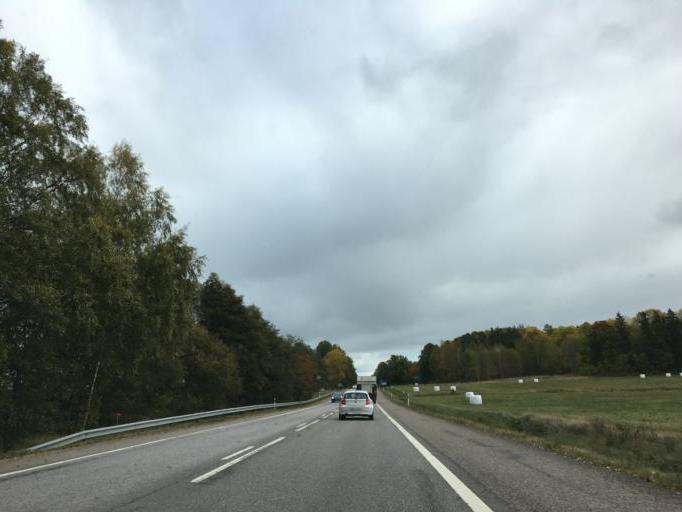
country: SE
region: Soedermanland
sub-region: Nykopings Kommun
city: Nykoping
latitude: 58.7694
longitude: 16.9548
